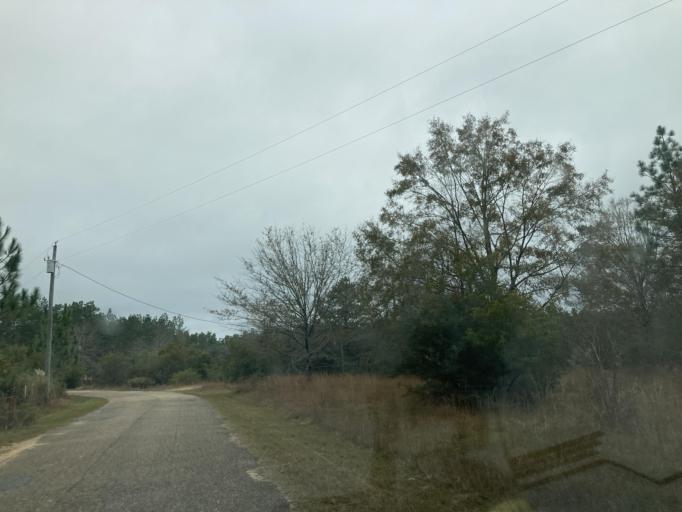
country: US
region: Mississippi
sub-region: Lamar County
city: Lumberton
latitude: 31.0180
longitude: -89.4969
